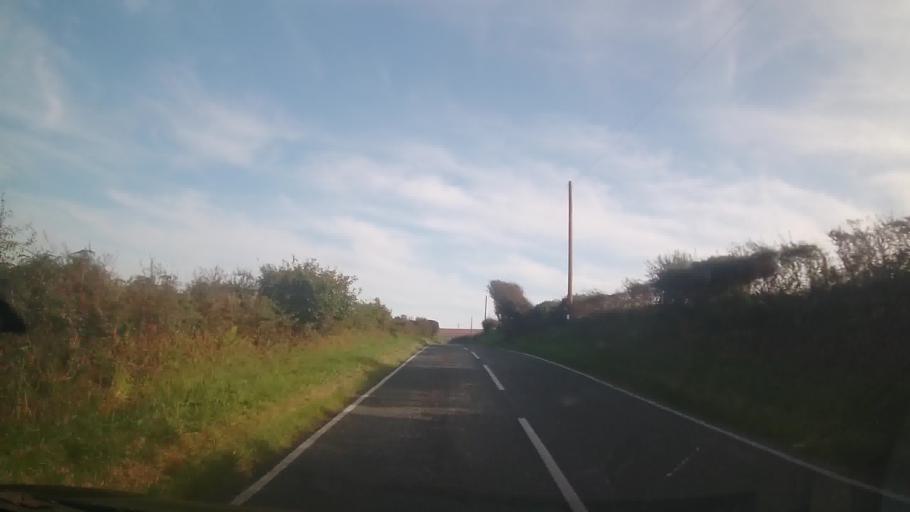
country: GB
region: Wales
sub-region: Pembrokeshire
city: Ambleston
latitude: 51.9692
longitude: -4.9045
